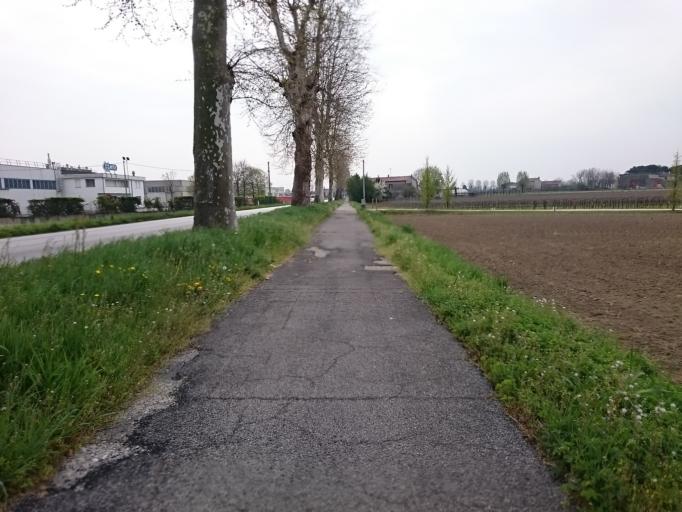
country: IT
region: Veneto
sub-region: Provincia di Padova
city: Bagnoli di Sopra
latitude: 45.2026
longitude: 11.8833
